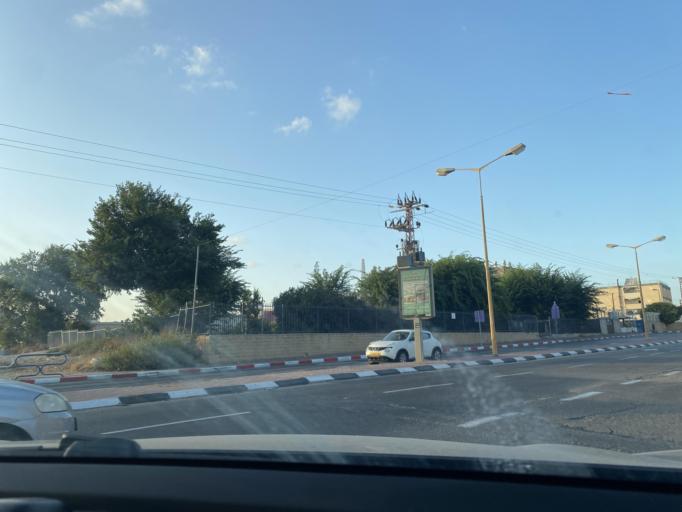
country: IL
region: Southern District
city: Ashdod
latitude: 31.8097
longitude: 34.6593
